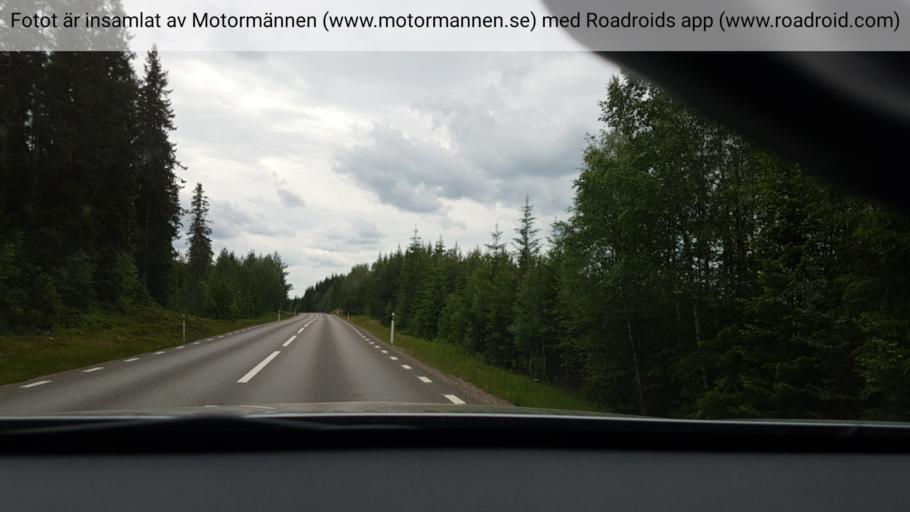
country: SE
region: Vaermland
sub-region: Torsby Kommun
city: Torsby
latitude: 60.3556
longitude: 13.1736
